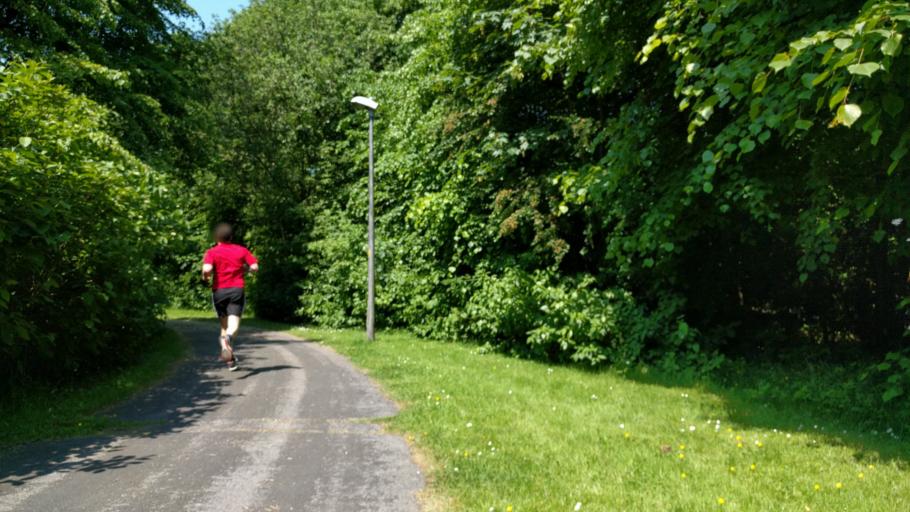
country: GB
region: England
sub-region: Warrington
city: Croft
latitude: 53.4290
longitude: -2.5314
